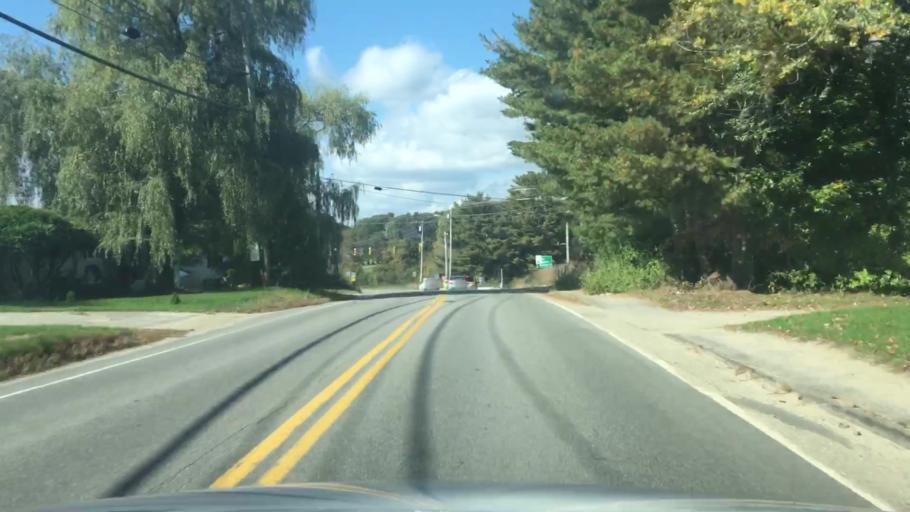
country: US
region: Maine
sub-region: Knox County
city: Warren
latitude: 44.1237
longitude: -69.2370
